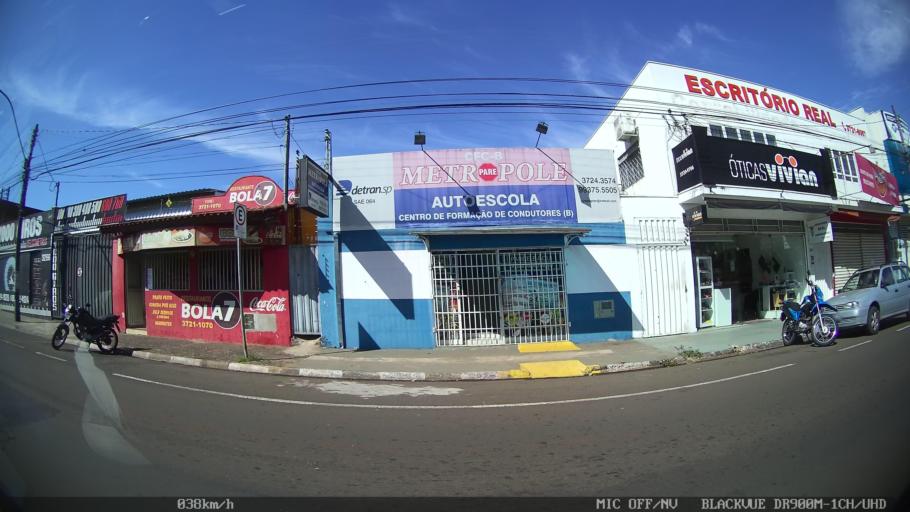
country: BR
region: Sao Paulo
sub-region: Franca
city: Franca
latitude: -20.5228
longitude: -47.4099
